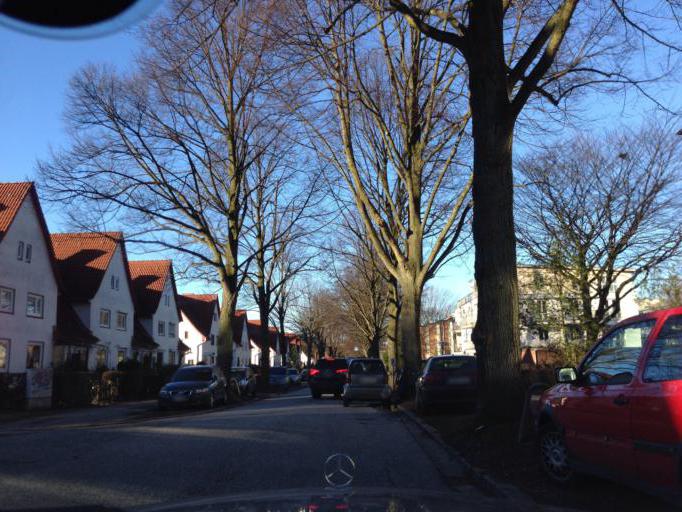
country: DE
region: Hamburg
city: Marienthal
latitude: 53.5878
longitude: 10.0845
